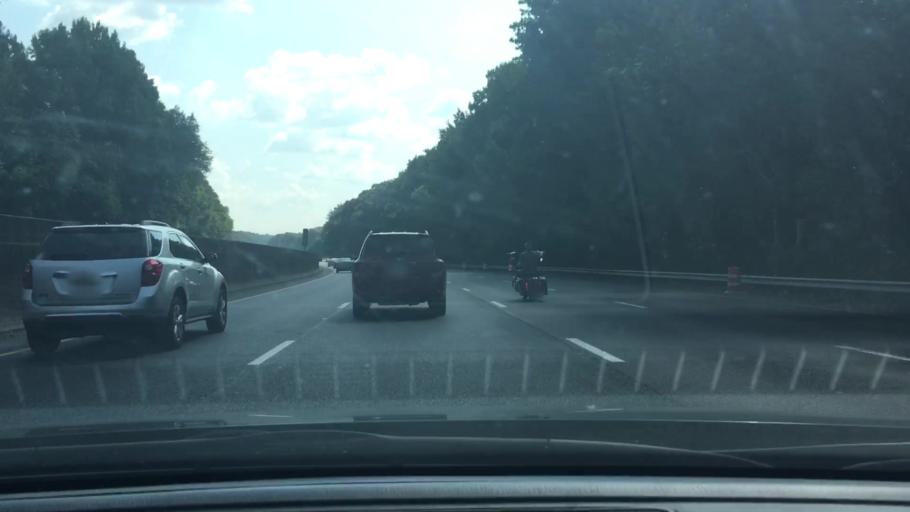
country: US
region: Georgia
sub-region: Clayton County
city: Forest Park
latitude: 33.6579
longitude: -84.3625
